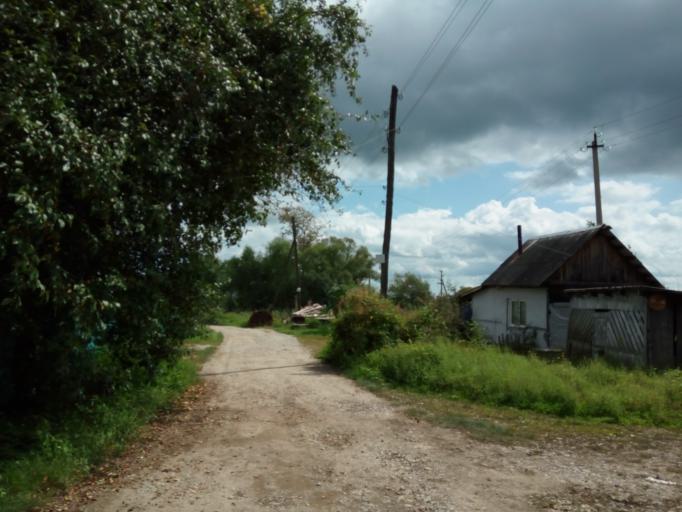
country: RU
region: Primorskiy
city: Dal'nerechensk
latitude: 45.9387
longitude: 133.8147
